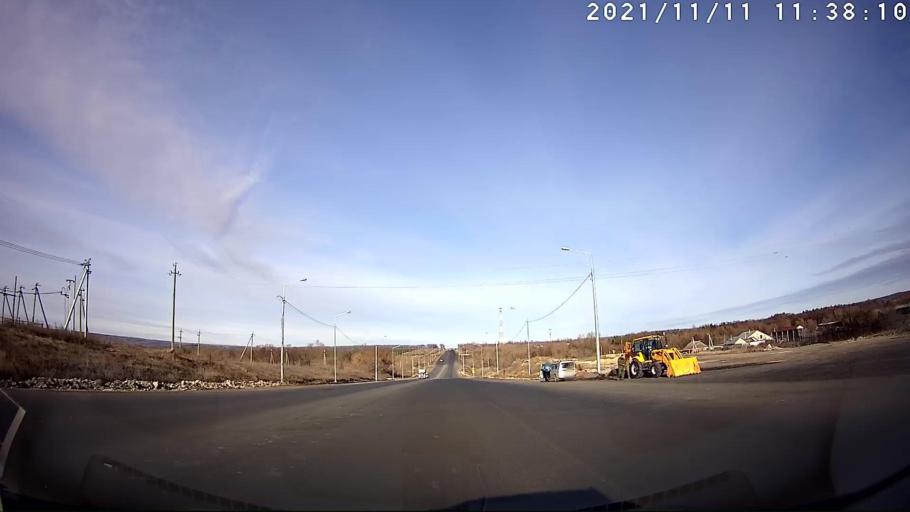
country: RU
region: Samara
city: Varlamovo
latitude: 53.3793
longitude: 48.3785
